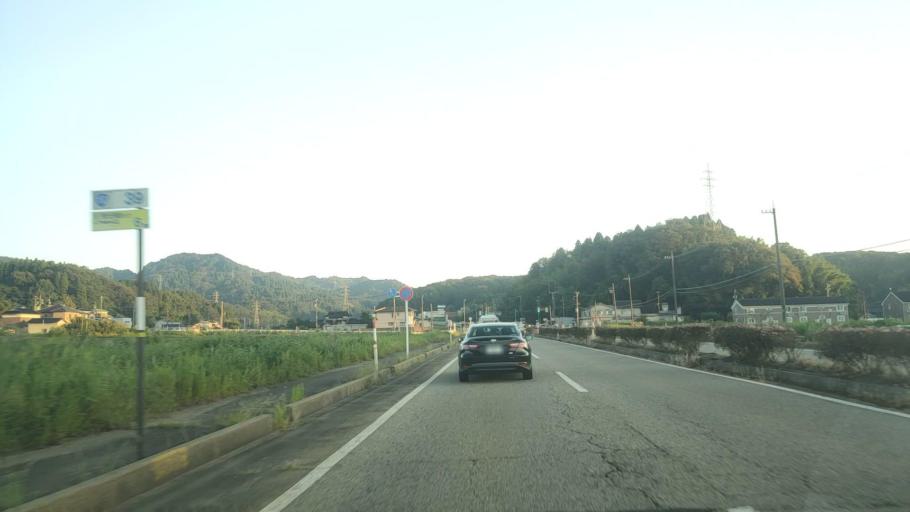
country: JP
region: Toyama
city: Himi
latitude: 36.8117
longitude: 136.9966
